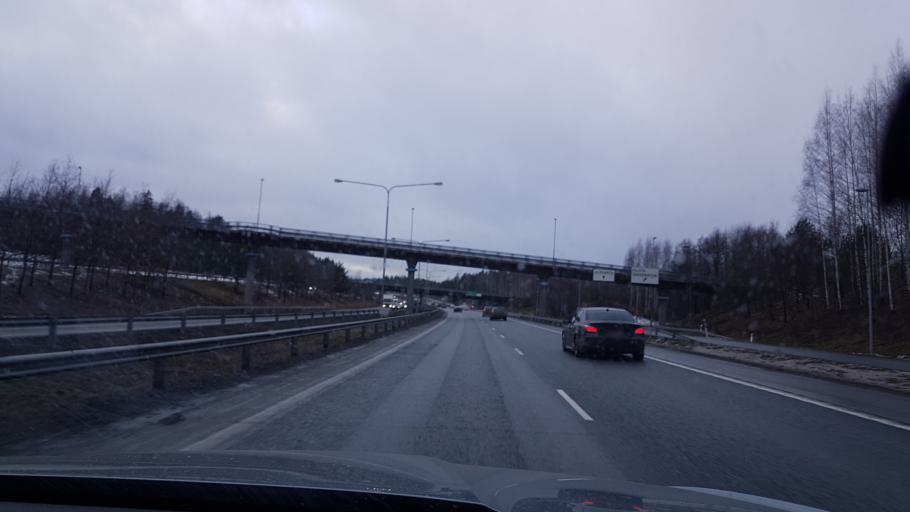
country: FI
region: Pirkanmaa
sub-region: Tampere
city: Tampere
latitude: 61.4702
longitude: 23.8470
